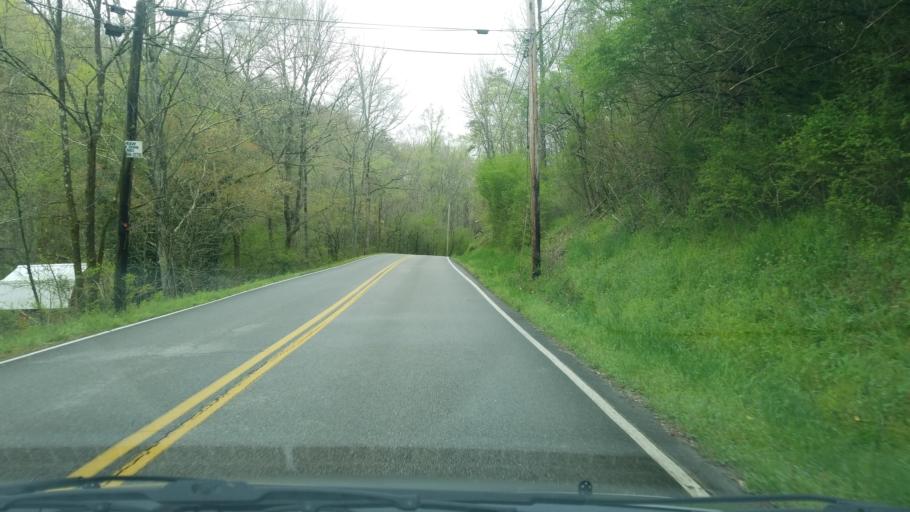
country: US
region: Tennessee
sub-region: Hamilton County
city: Collegedale
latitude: 35.0135
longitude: -85.0736
